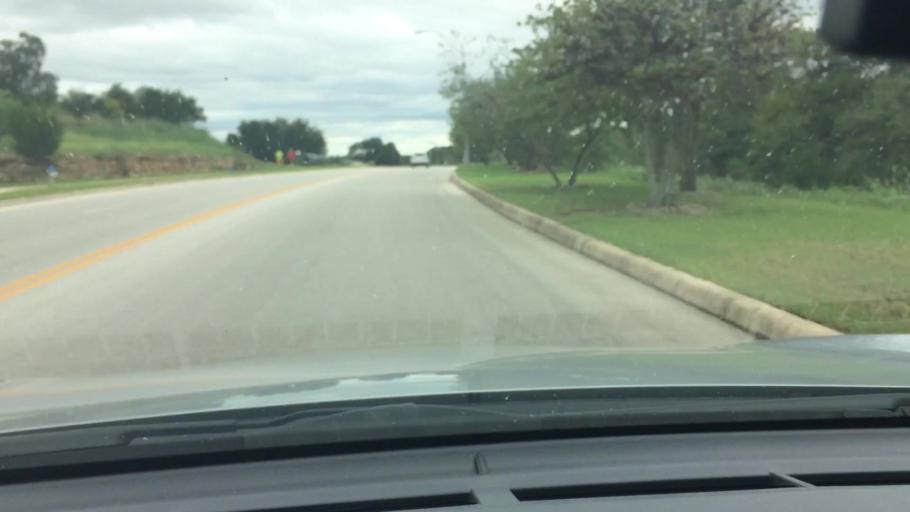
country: US
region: Texas
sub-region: Bexar County
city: Timberwood Park
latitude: 29.6613
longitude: -98.4010
